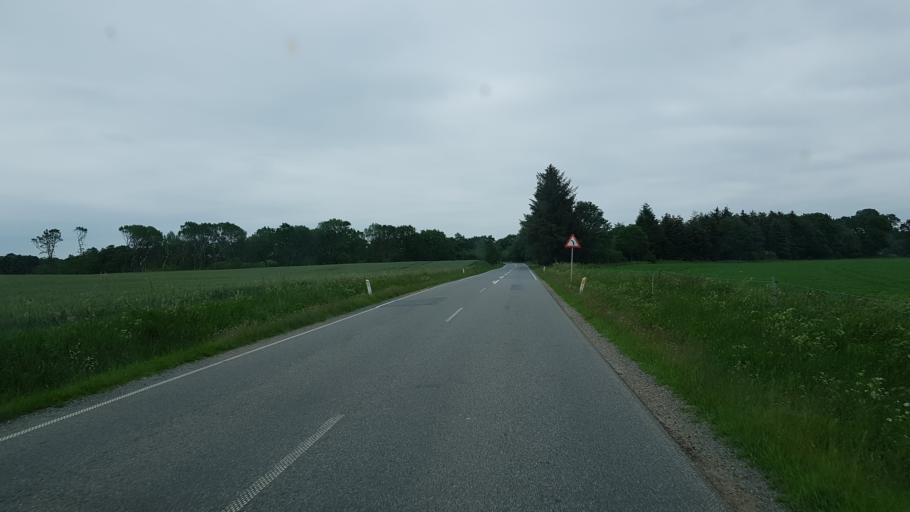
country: DK
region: South Denmark
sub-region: Varde Kommune
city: Olgod
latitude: 55.7214
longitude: 8.7168
